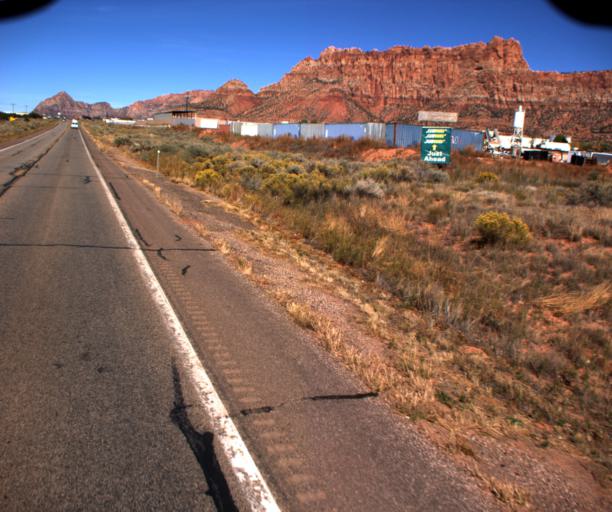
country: US
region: Arizona
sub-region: Mohave County
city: Colorado City
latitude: 36.9935
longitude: -112.9934
